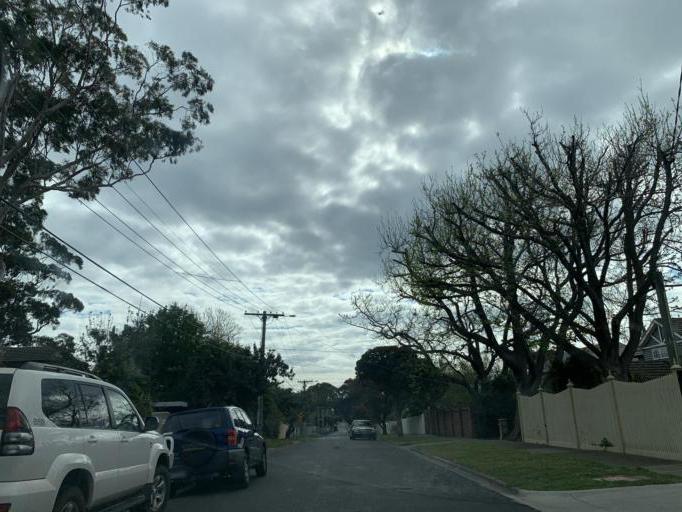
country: AU
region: Victoria
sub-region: Bayside
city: Black Rock
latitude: -37.9742
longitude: 145.0254
